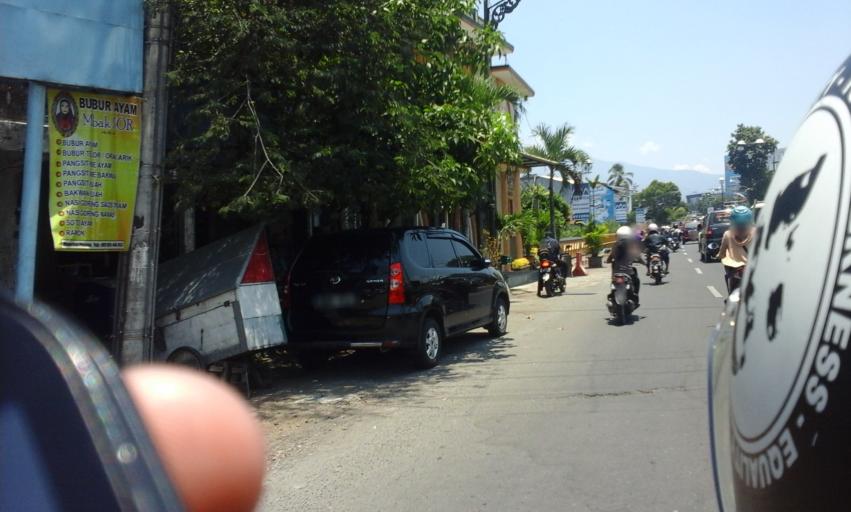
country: ID
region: East Java
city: Kepatihan
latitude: -8.1780
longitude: 113.7044
